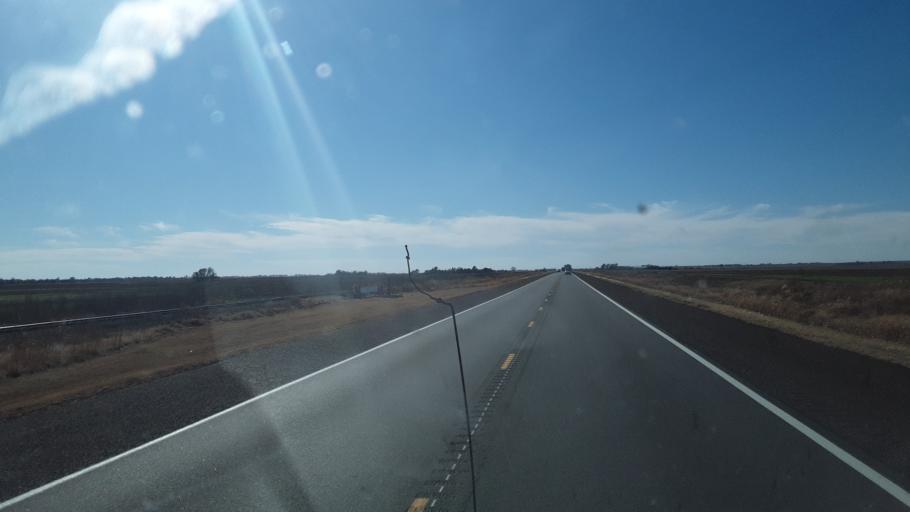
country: US
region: Kansas
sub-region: Barton County
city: Great Bend
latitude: 38.3004
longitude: -98.9065
